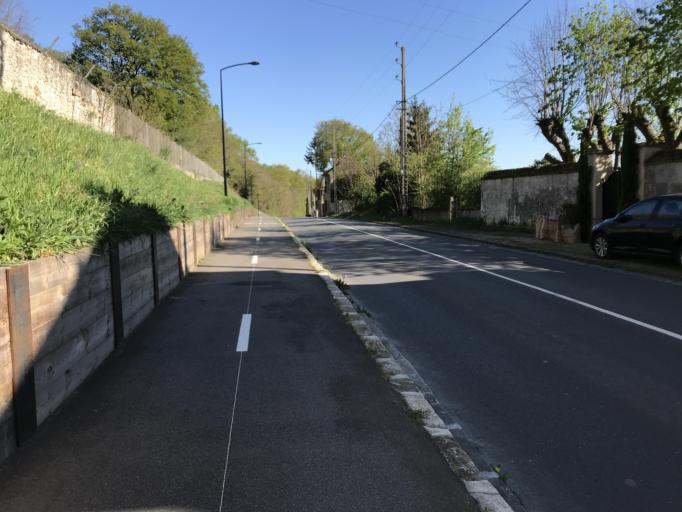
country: FR
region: Ile-de-France
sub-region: Departement de l'Essonne
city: Marcoussis
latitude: 48.6533
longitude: 2.2127
